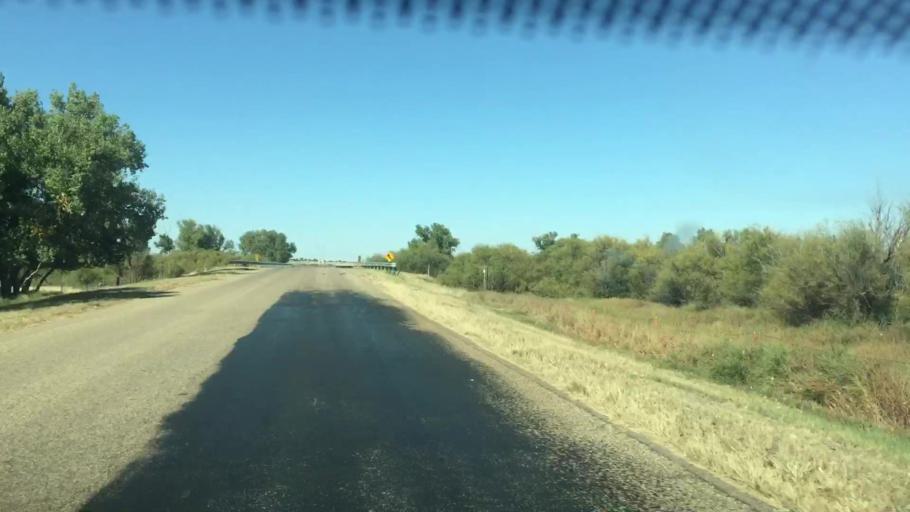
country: US
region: Colorado
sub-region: Prowers County
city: Lamar
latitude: 38.0954
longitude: -102.5195
